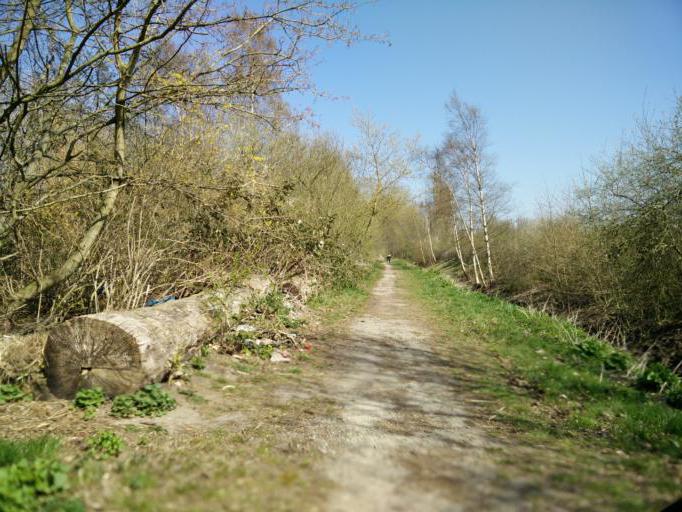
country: DE
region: Mecklenburg-Vorpommern
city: Lambrechtshagen
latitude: 54.1309
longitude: 12.0405
